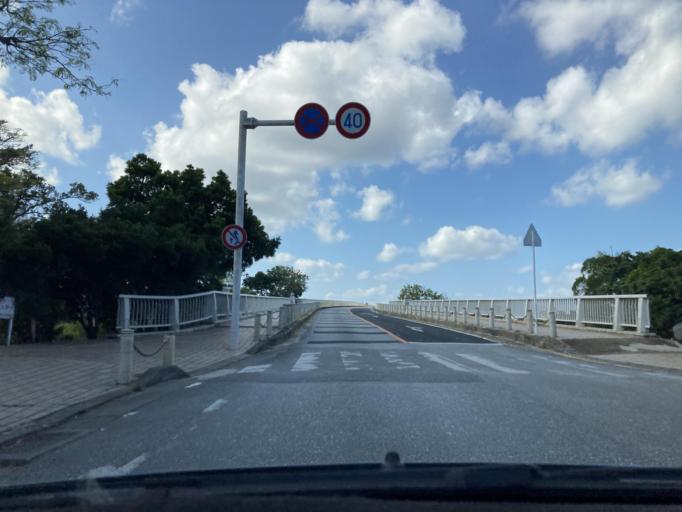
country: JP
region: Okinawa
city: Tomigusuku
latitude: 26.1962
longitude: 127.6893
